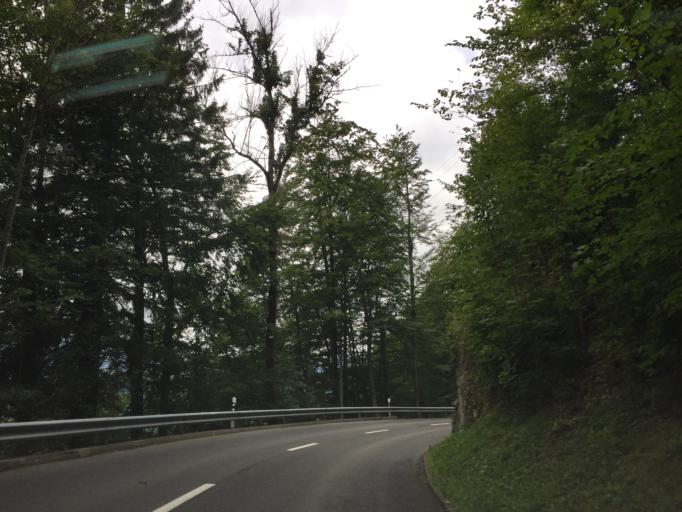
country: CH
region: Obwalden
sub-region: Obwalden
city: Kerns
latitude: 46.8633
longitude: 8.2789
